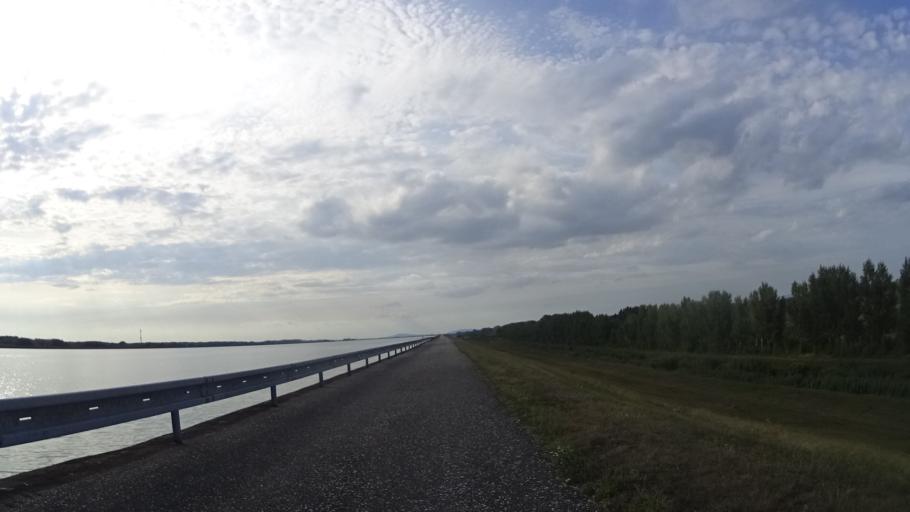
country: HU
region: Gyor-Moson-Sopron
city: Halaszi
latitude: 47.9589
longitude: 17.4264
